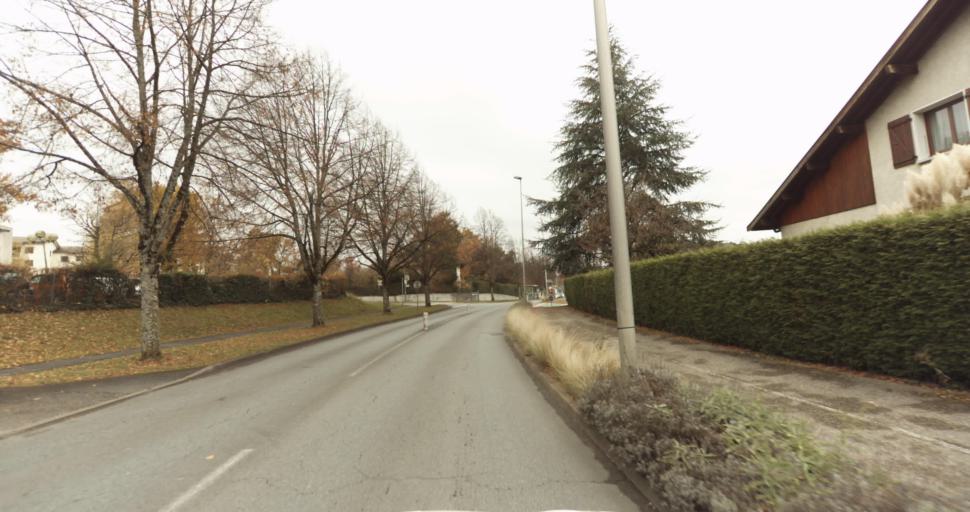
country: FR
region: Rhone-Alpes
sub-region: Departement de la Haute-Savoie
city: Cran-Gevrier
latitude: 45.8829
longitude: 6.1066
